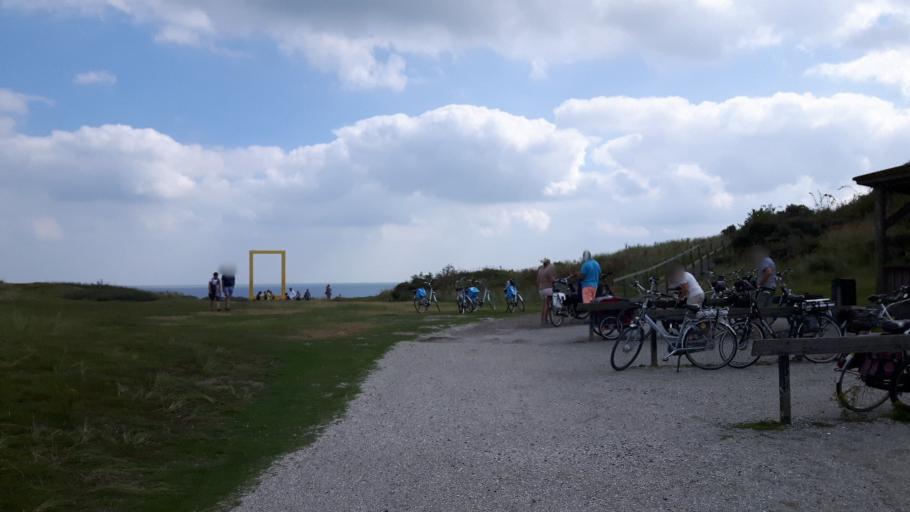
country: NL
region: Friesland
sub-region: Gemeente Dongeradeel
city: Holwerd
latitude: 53.4584
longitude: 5.9024
